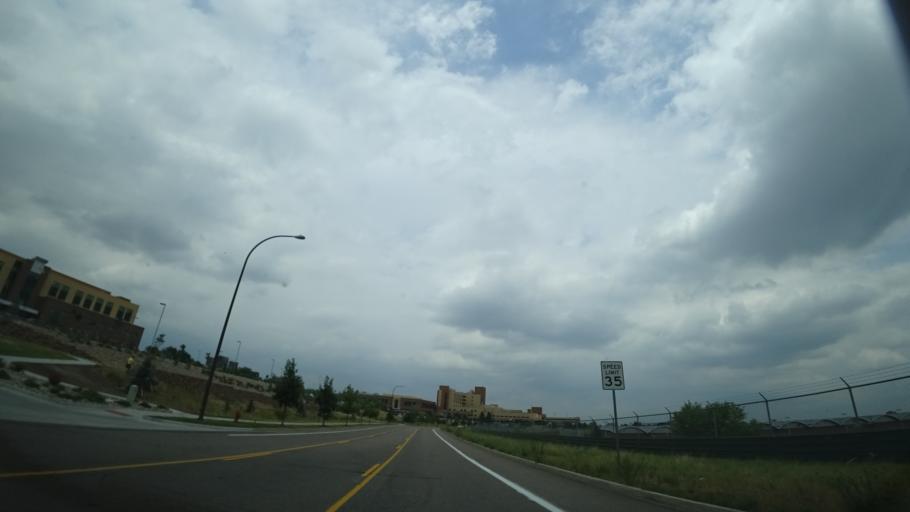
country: US
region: Colorado
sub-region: Jefferson County
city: Lakewood
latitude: 39.7118
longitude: -105.1279
